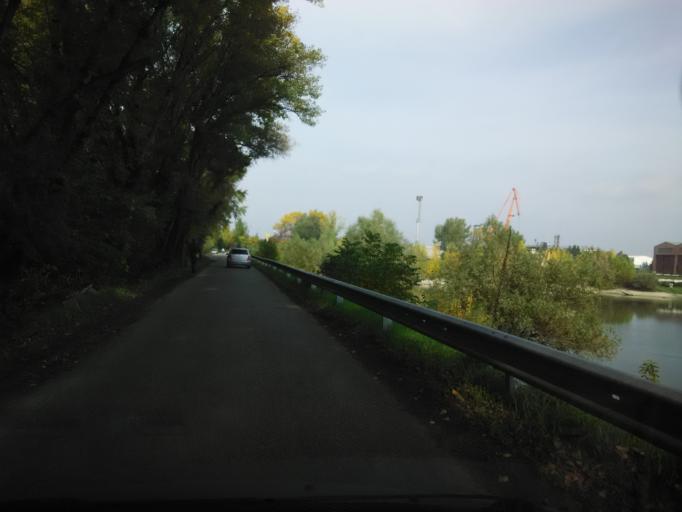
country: SK
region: Nitriansky
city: Komarno
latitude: 47.7583
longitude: 18.0966
